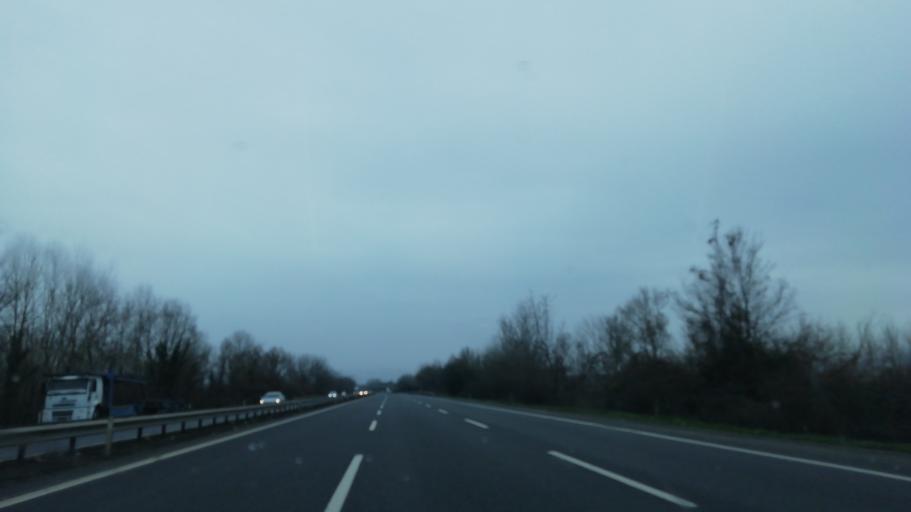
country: TR
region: Sakarya
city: Karapurcek
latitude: 40.7160
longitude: 30.4863
